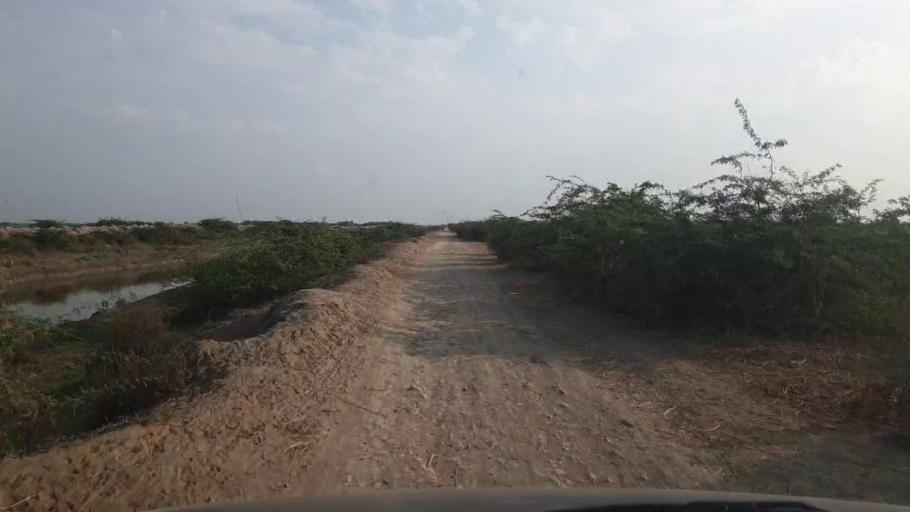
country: PK
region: Sindh
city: Badin
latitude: 24.5558
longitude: 68.6697
